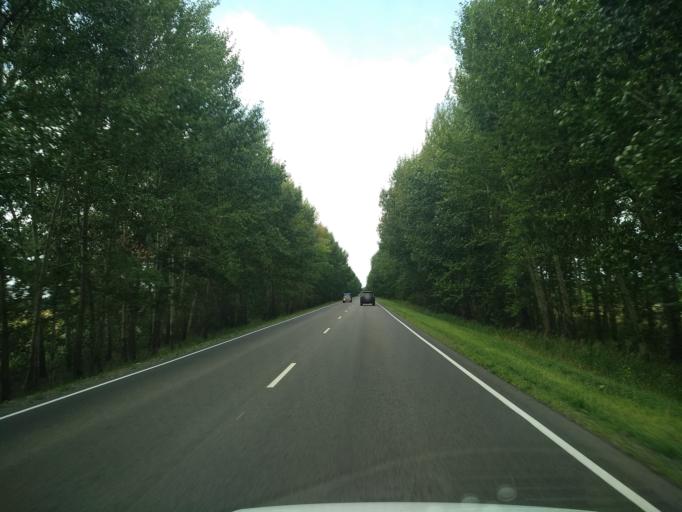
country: RU
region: Voronezj
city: Pereleshino
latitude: 51.8022
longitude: 40.1780
